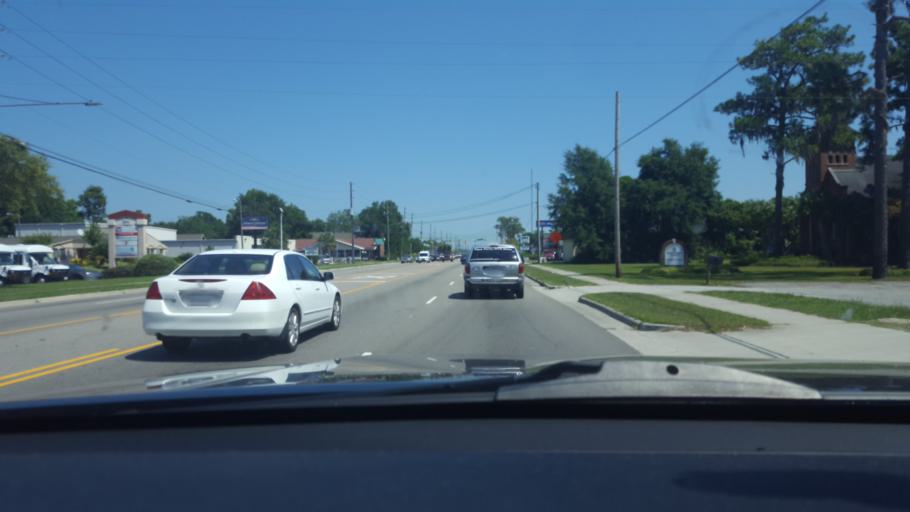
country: US
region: North Carolina
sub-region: New Hanover County
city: Kings Grant
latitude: 34.2412
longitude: -77.8986
